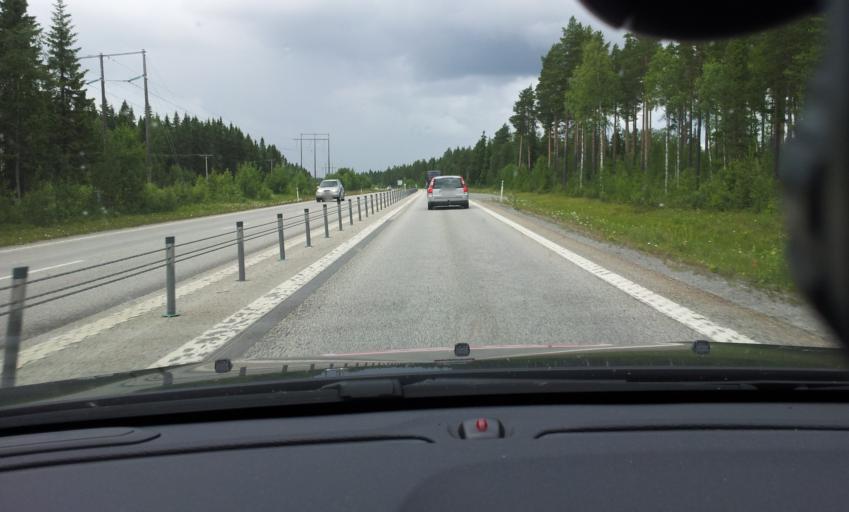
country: SE
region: Jaemtland
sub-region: OEstersunds Kommun
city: Brunflo
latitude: 63.1490
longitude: 14.7762
